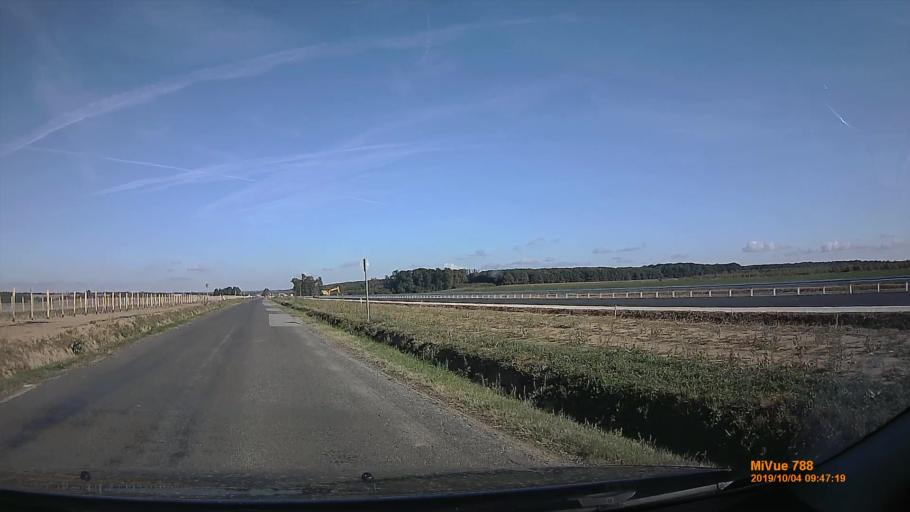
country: HU
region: Somogy
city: Kaposvar
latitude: 46.4291
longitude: 17.7734
